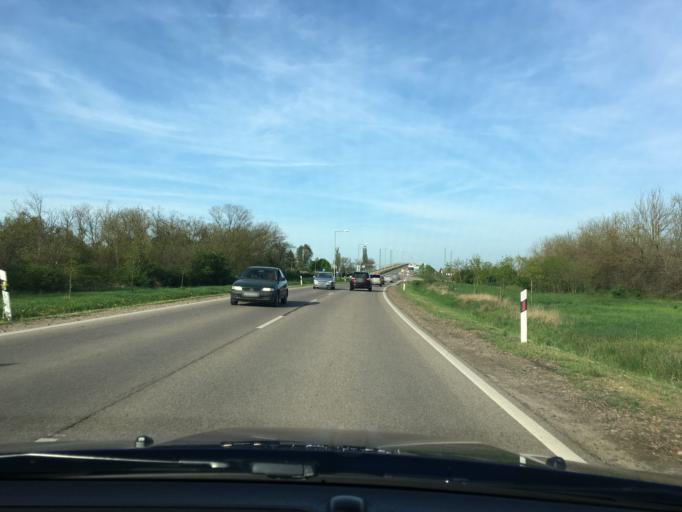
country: HU
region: Bekes
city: Mezobereny
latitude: 46.8096
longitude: 21.0102
